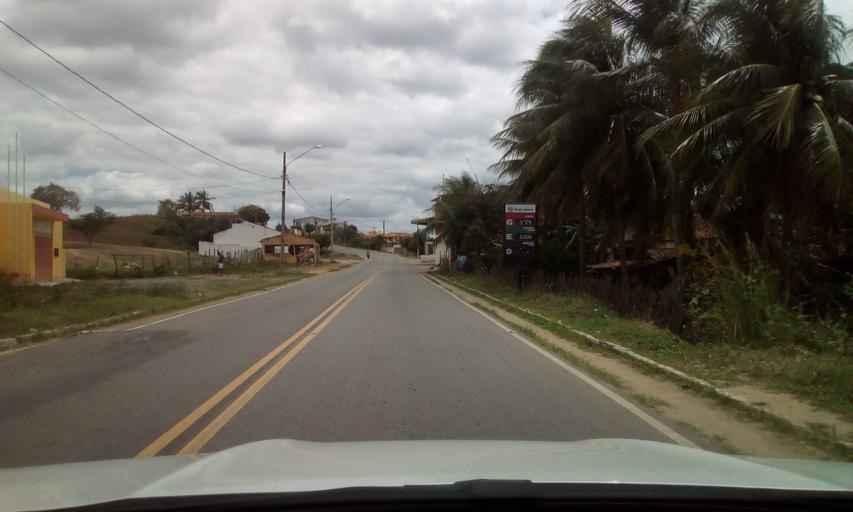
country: BR
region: Paraiba
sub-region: Serra Redonda
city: Alagoa Grande
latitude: -7.1695
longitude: -35.5917
